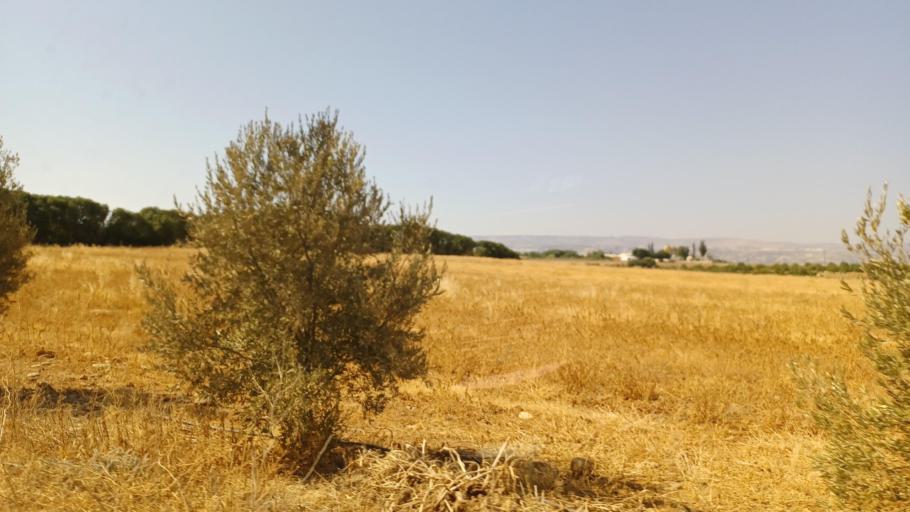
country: CY
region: Pafos
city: Polis
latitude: 35.0479
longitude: 32.4546
